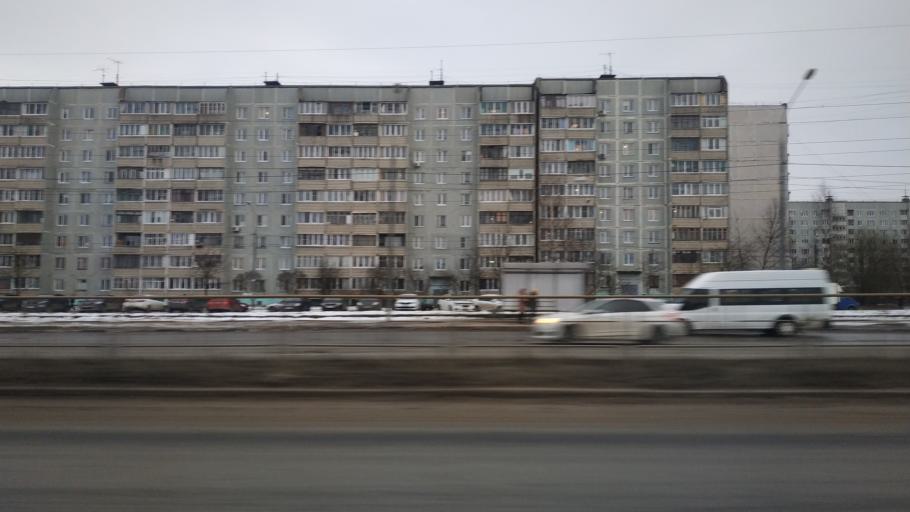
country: RU
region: Tverskaya
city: Tver
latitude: 56.8211
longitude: 35.8880
